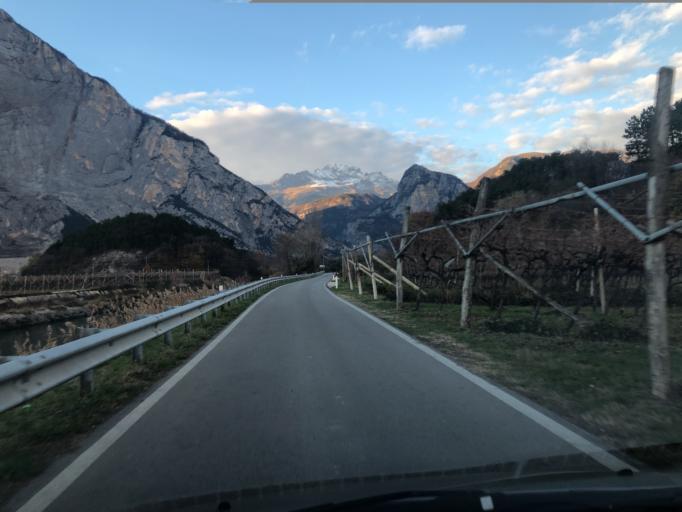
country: IT
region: Trentino-Alto Adige
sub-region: Provincia di Trento
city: Pietramurata
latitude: 46.0182
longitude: 10.9585
